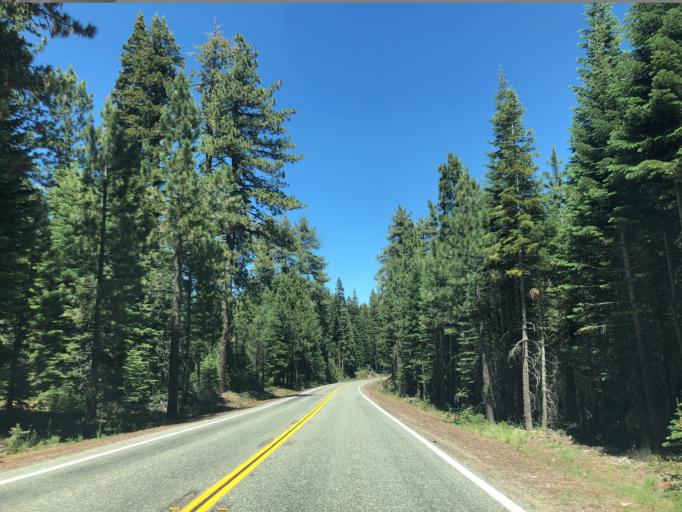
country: US
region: California
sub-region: Shasta County
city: Burney
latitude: 40.5786
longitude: -121.5644
